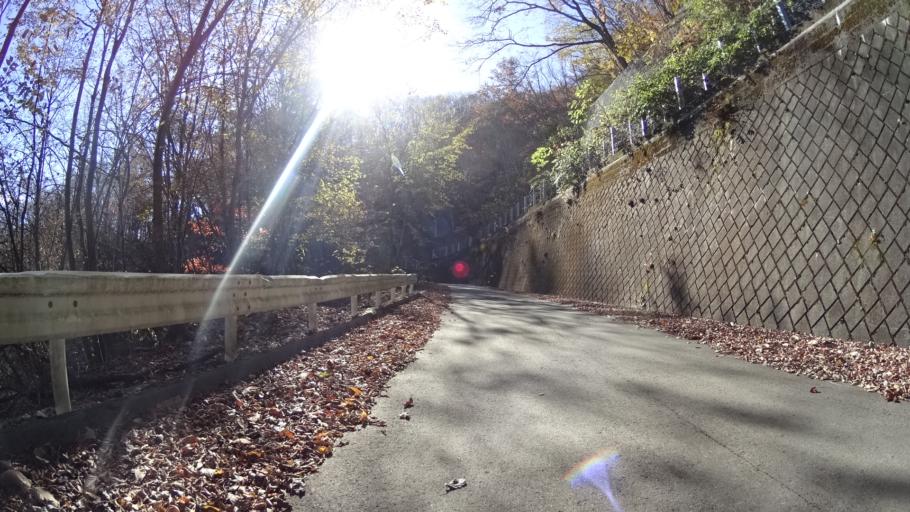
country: JP
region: Yamanashi
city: Otsuki
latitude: 35.7309
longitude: 138.9469
